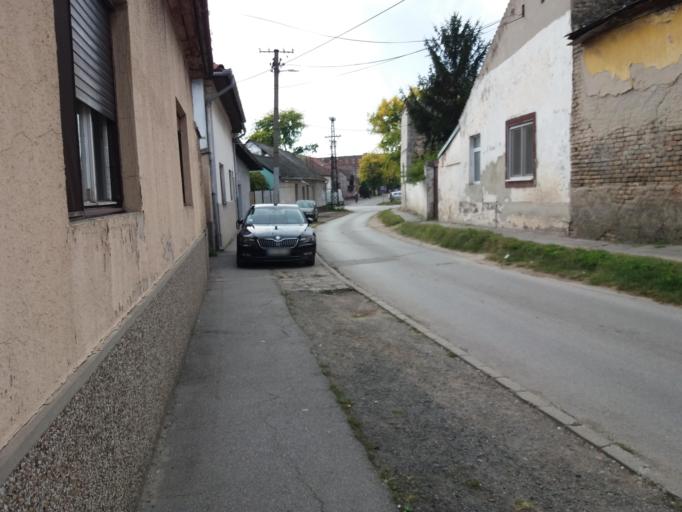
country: RS
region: Autonomna Pokrajina Vojvodina
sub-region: Severnobacki Okrug
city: Subotica
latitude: 46.1056
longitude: 19.6638
